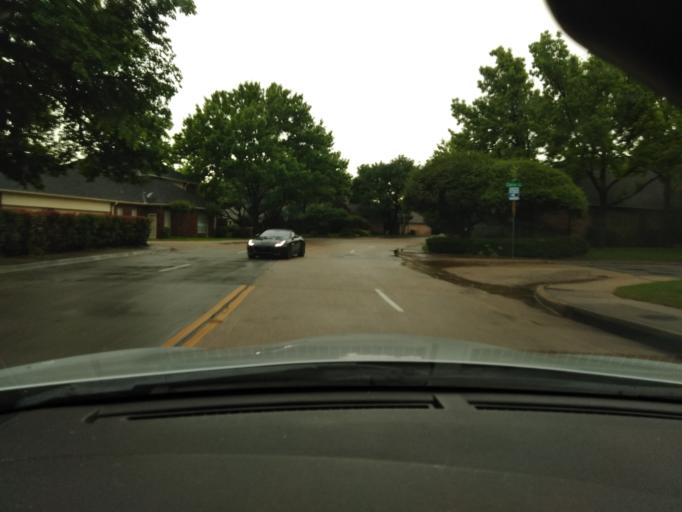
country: US
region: Texas
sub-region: Dallas County
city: Addison
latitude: 32.9909
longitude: -96.7804
